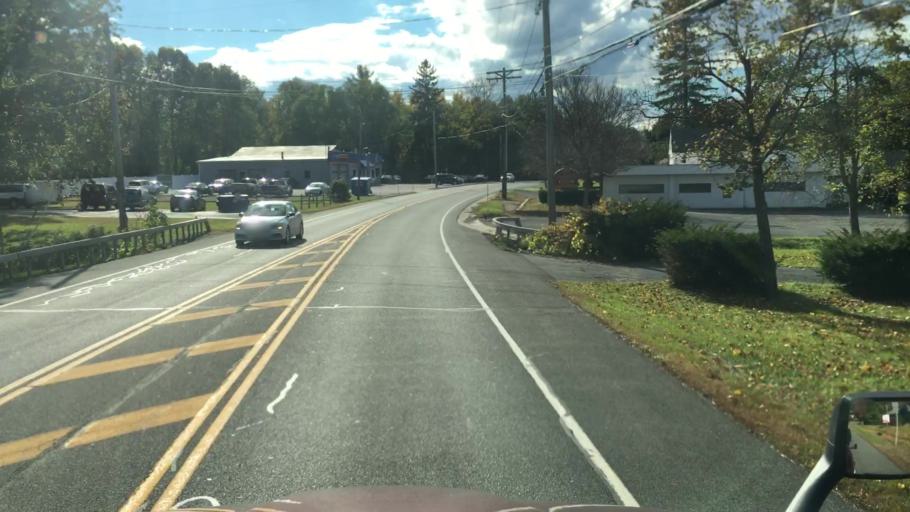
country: US
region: New York
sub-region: Schenectady County
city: East Glenville
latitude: 42.8968
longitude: -73.9124
